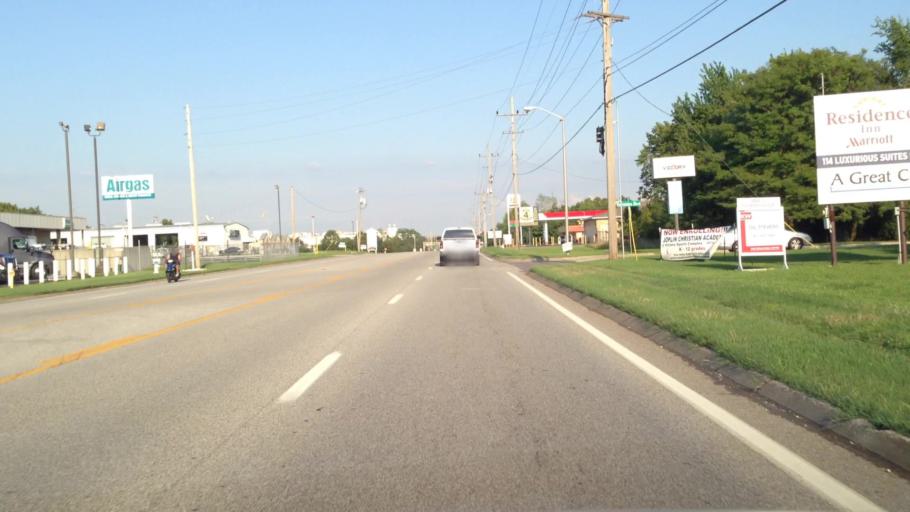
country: US
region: Missouri
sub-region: Jasper County
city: Duquesne
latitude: 37.0551
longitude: -94.4756
